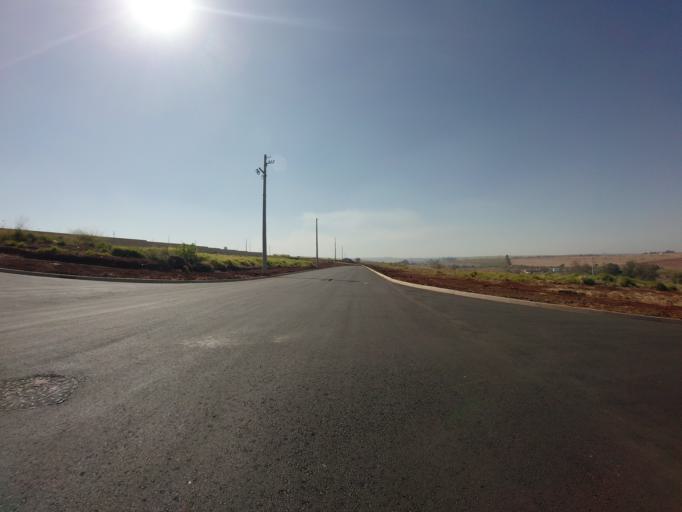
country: BR
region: Sao Paulo
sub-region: Piracicaba
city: Piracicaba
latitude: -22.7627
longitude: -47.5818
